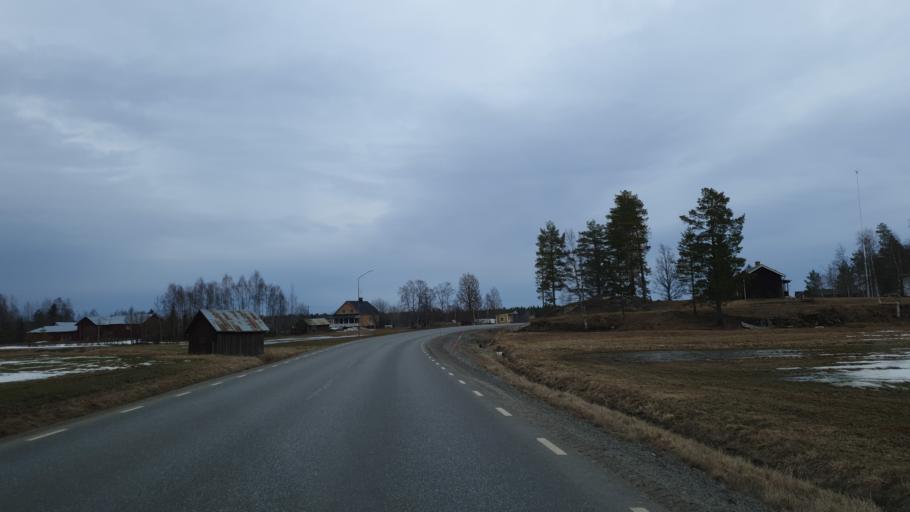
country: SE
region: Vaesterbotten
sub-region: Robertsfors Kommun
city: Robertsfors
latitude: 64.2301
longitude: 20.9474
